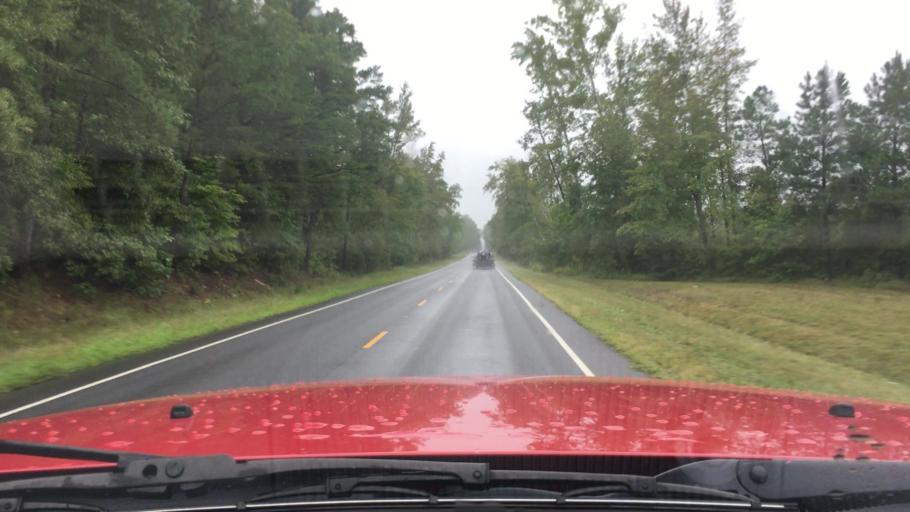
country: US
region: Virginia
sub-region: Caroline County
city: Bowling Green
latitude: 37.9680
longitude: -77.3419
